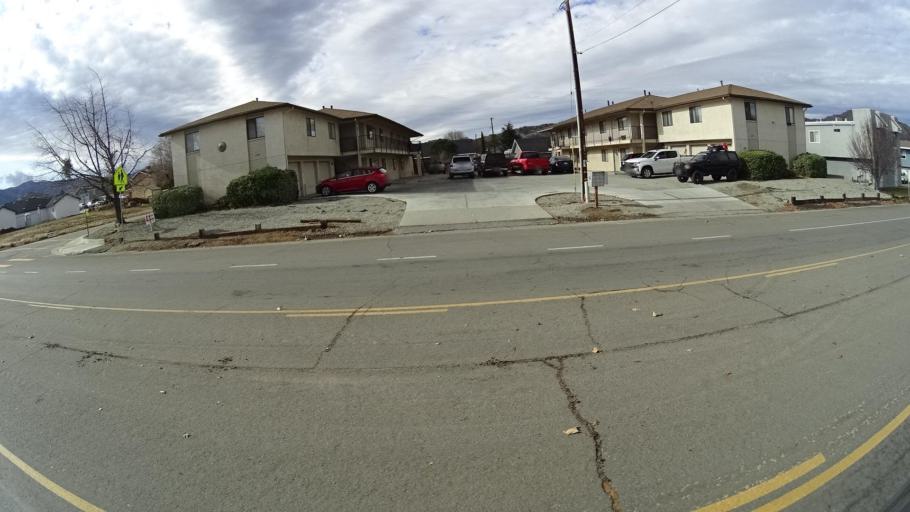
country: US
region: California
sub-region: Kern County
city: Golden Hills
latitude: 35.1288
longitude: -118.4860
